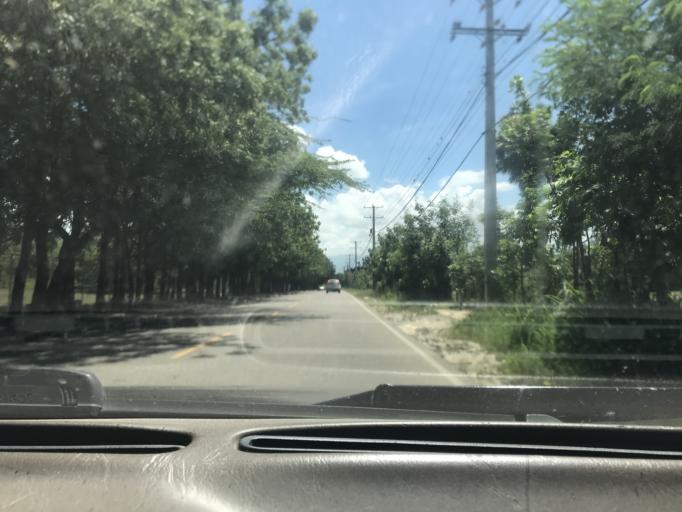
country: DO
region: Santiago
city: Santiago de los Caballeros
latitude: 19.4066
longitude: -70.7210
